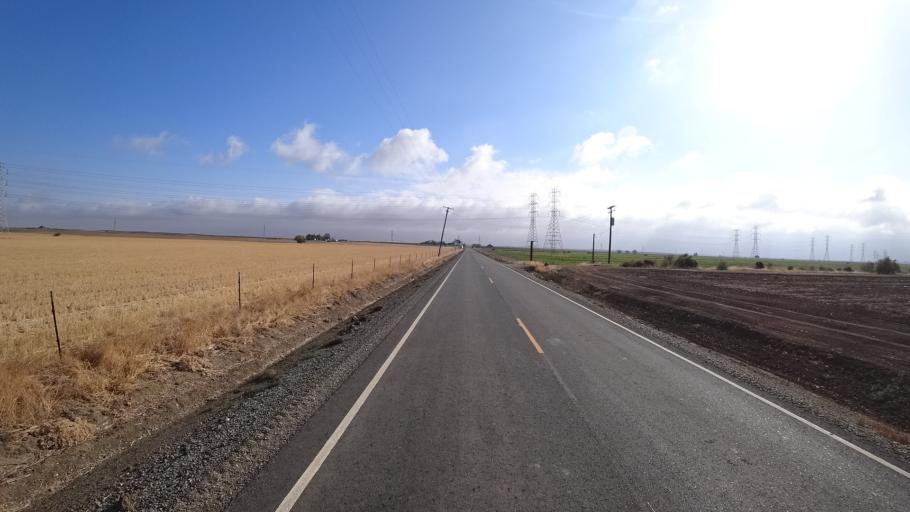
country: US
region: California
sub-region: Yolo County
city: Esparto
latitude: 38.7810
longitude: -122.0169
